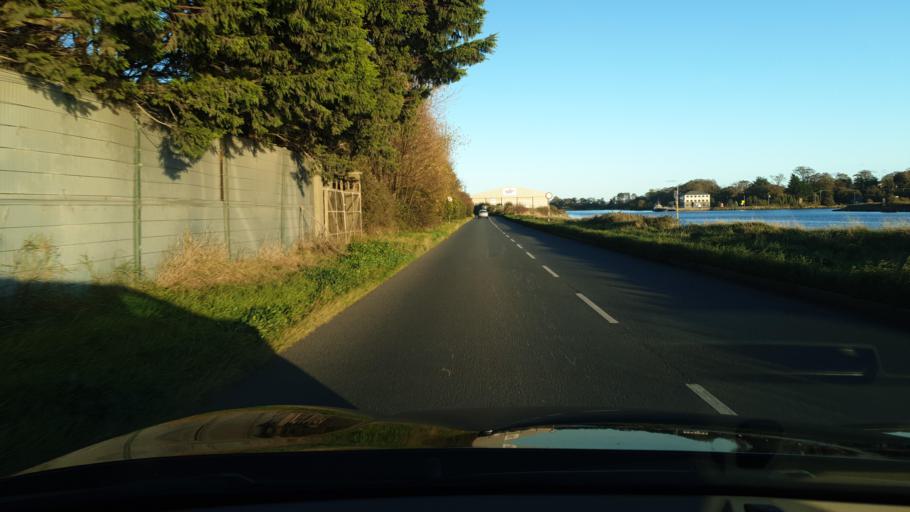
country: IE
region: Leinster
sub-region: Lu
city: Drogheda
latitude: 53.7210
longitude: -6.3151
